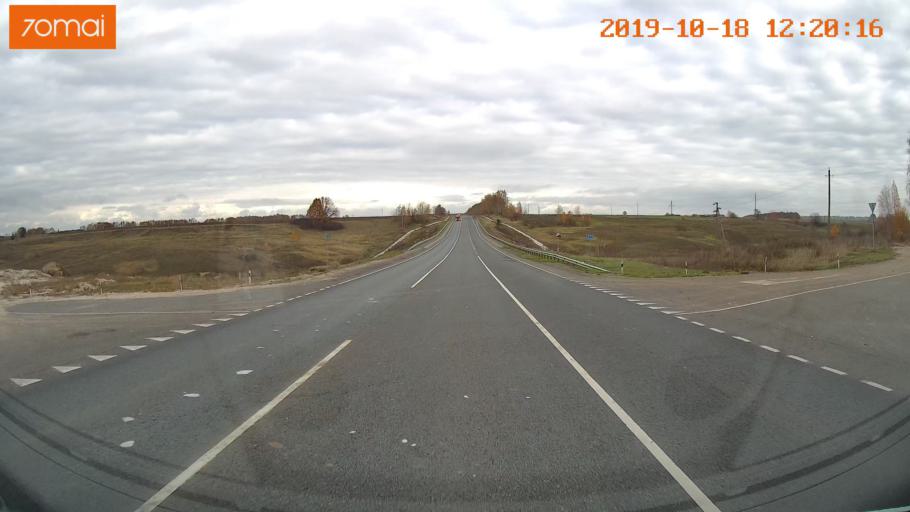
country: RU
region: Rjazan
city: Bagramovo
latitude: 54.4949
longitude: 39.4780
